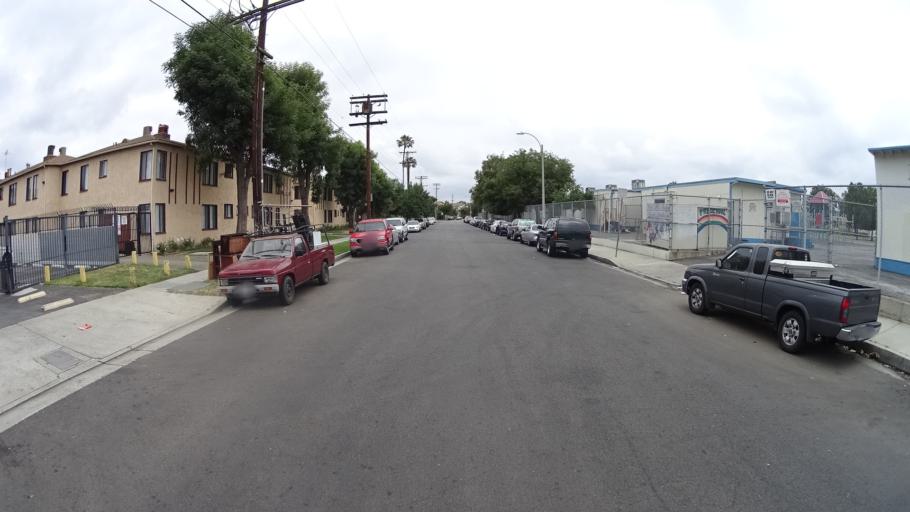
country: US
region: California
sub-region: Los Angeles County
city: San Fernando
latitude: 34.2404
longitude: -118.4471
